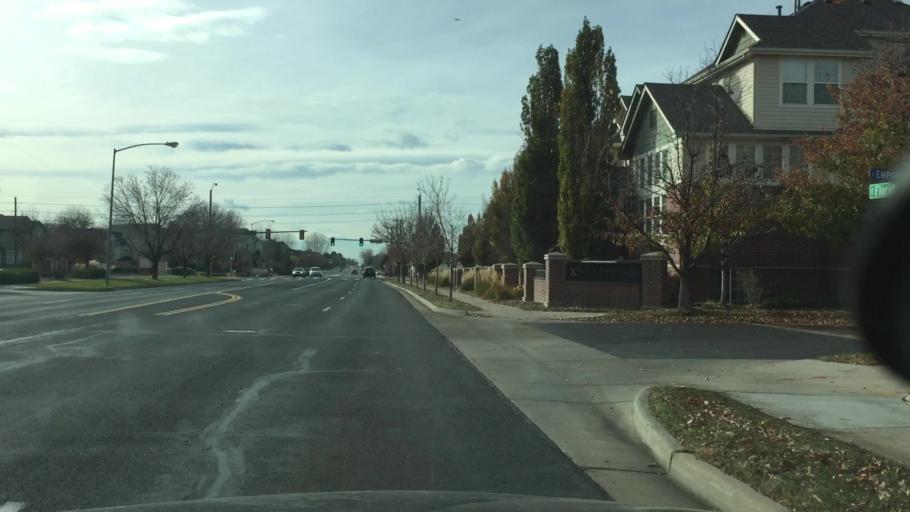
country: US
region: Colorado
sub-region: Adams County
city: Aurora
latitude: 39.6893
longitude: -104.8738
